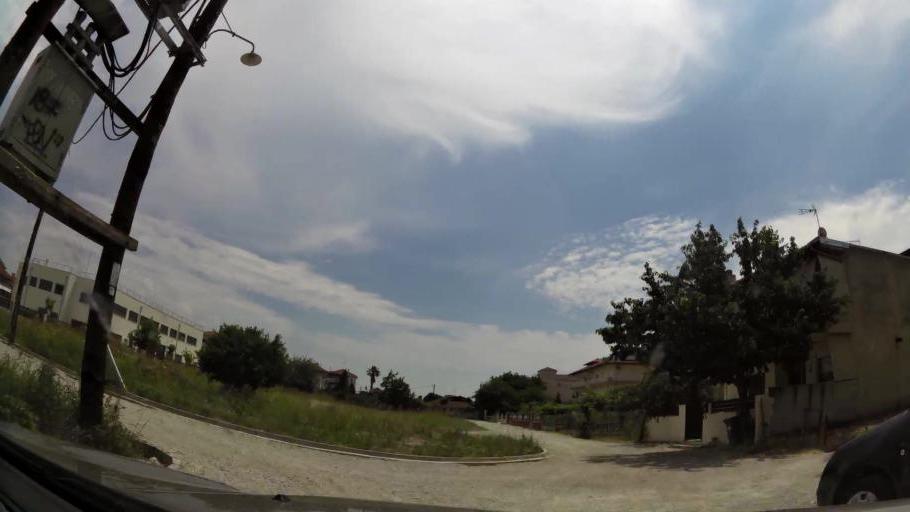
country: GR
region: Central Macedonia
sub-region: Nomos Pierias
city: Katerini
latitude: 40.2656
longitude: 22.5177
